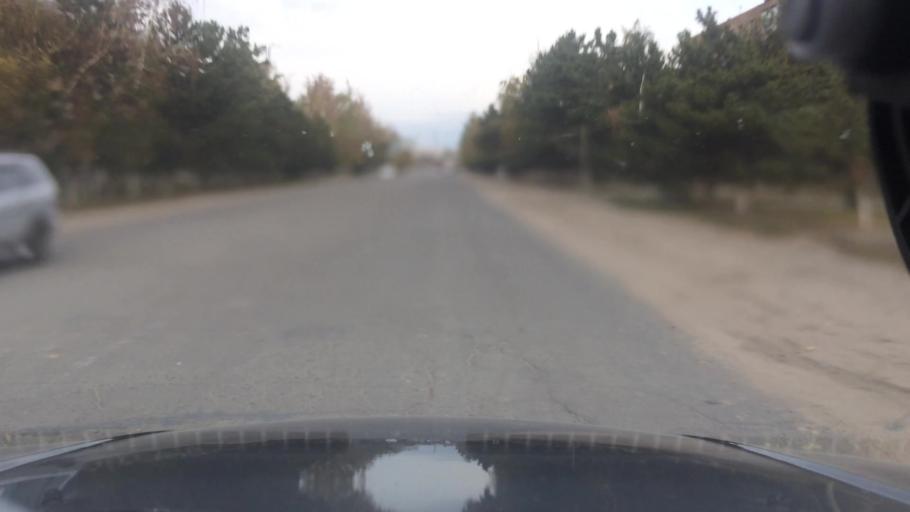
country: KG
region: Ysyk-Koel
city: Karakol
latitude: 42.4971
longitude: 78.3903
